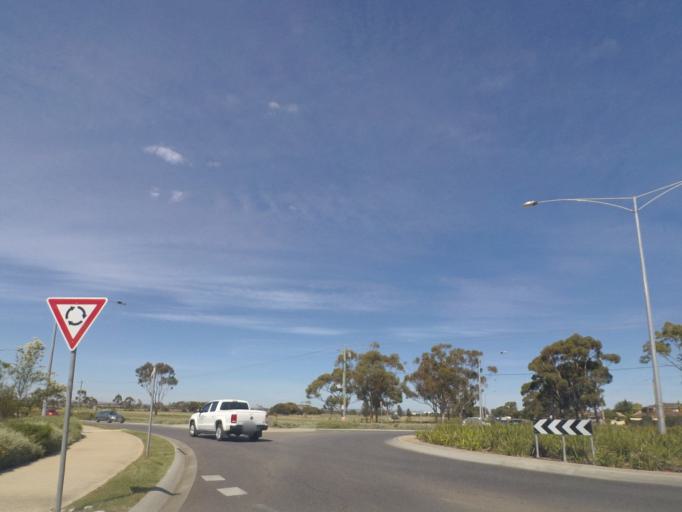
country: AU
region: Victoria
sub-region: Melton
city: Brookfield
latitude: -37.6857
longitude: 144.5498
